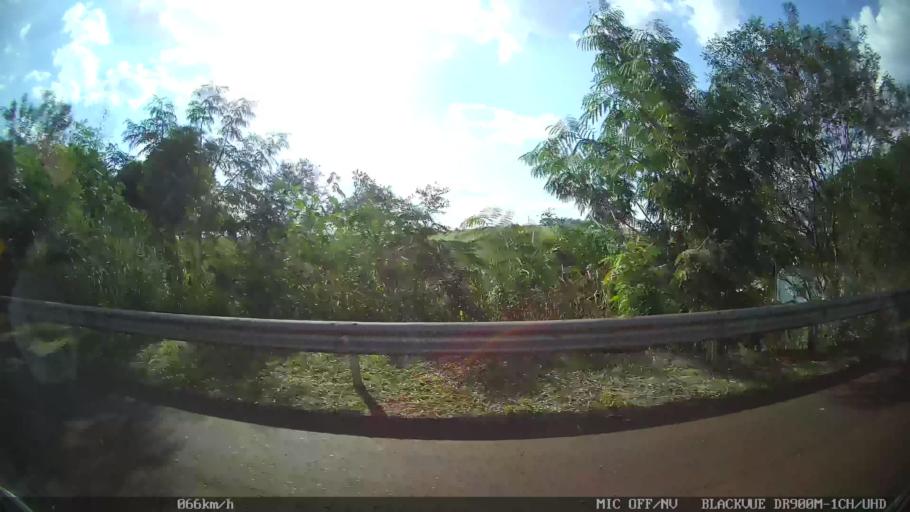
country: BR
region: Sao Paulo
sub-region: Ribeirao Preto
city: Ribeirao Preto
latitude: -21.1960
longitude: -47.8742
